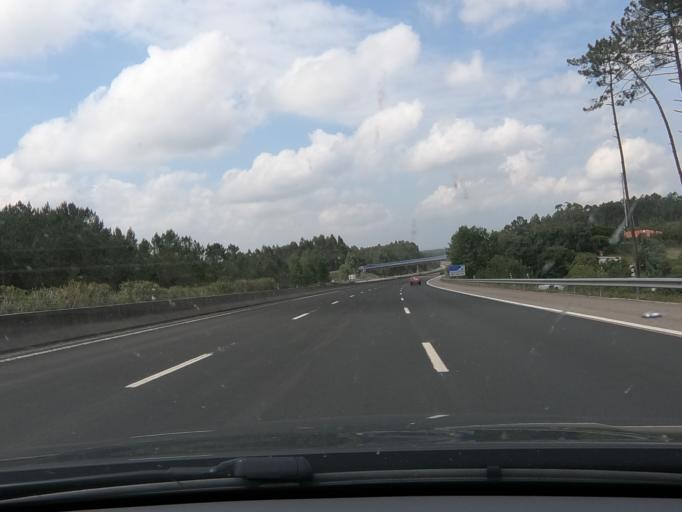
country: PT
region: Leiria
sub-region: Leiria
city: Maceira
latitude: 39.6791
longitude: -8.9395
